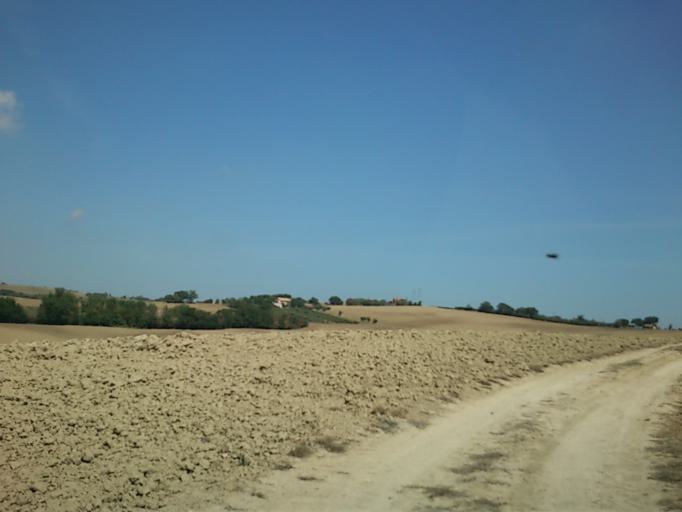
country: IT
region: The Marches
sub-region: Provincia di Pesaro e Urbino
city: Lucrezia
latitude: 43.7814
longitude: 12.9235
